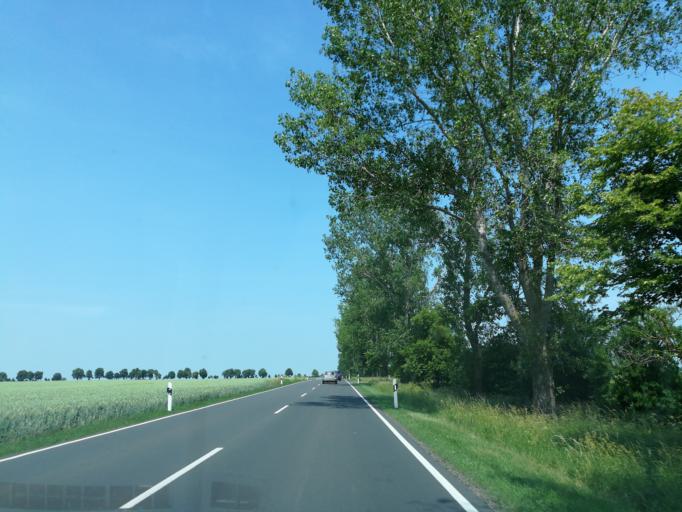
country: DE
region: Saxony-Anhalt
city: Gross Bornecke
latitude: 51.8403
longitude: 11.4555
